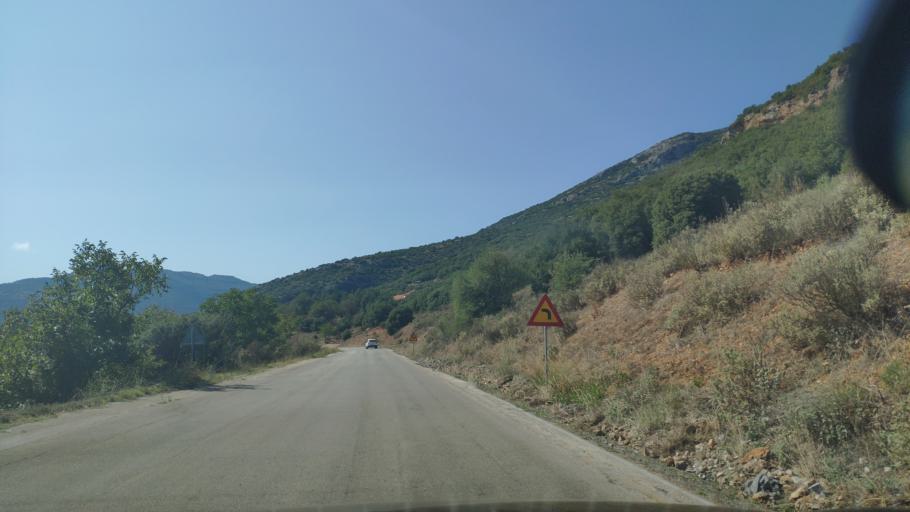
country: GR
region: Peloponnese
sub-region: Nomos Korinthias
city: Nemea
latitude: 37.9097
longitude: 22.5238
